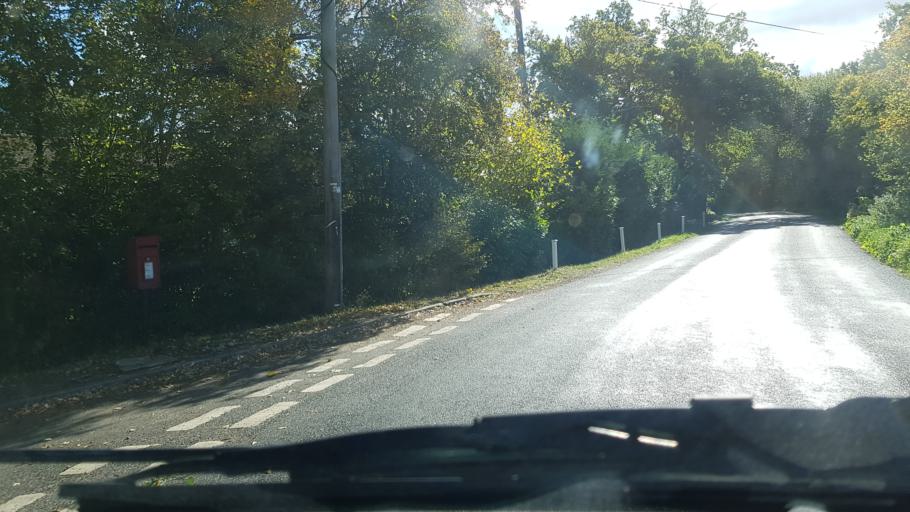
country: GB
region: England
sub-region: Surrey
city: Chiddingfold
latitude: 51.0699
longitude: -0.5471
